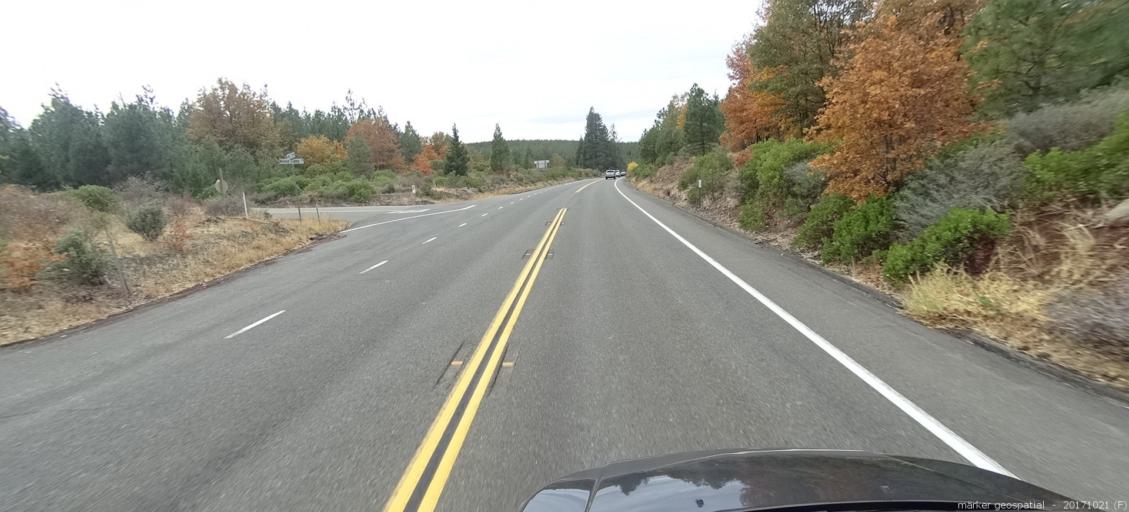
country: US
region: California
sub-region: Shasta County
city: Burney
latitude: 40.8660
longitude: -121.8487
